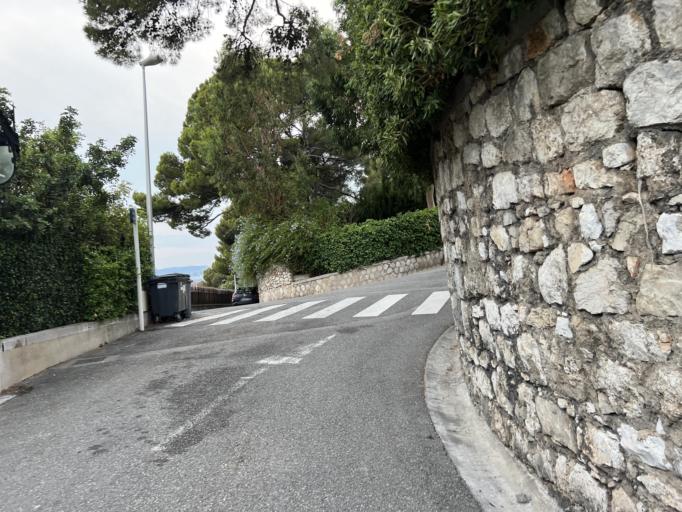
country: FR
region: Provence-Alpes-Cote d'Azur
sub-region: Departement des Alpes-Maritimes
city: Cap-d'Ail
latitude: 43.7207
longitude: 7.3974
